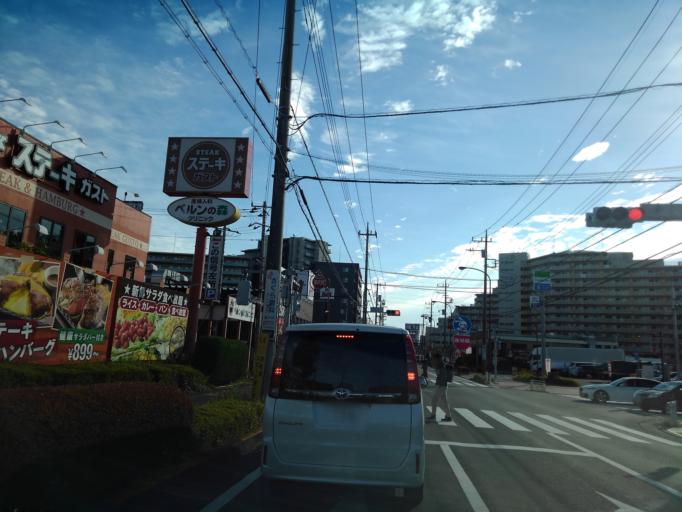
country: JP
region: Tokyo
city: Hachioji
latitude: 35.6032
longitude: 139.3644
